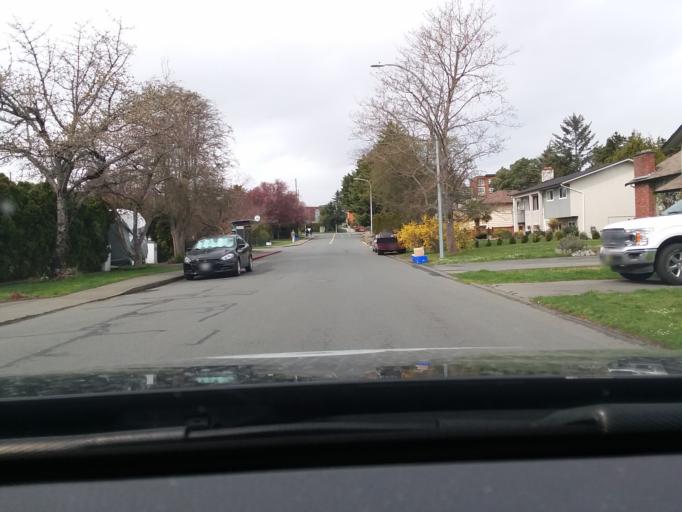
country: CA
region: British Columbia
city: Oak Bay
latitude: 48.4728
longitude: -123.3305
